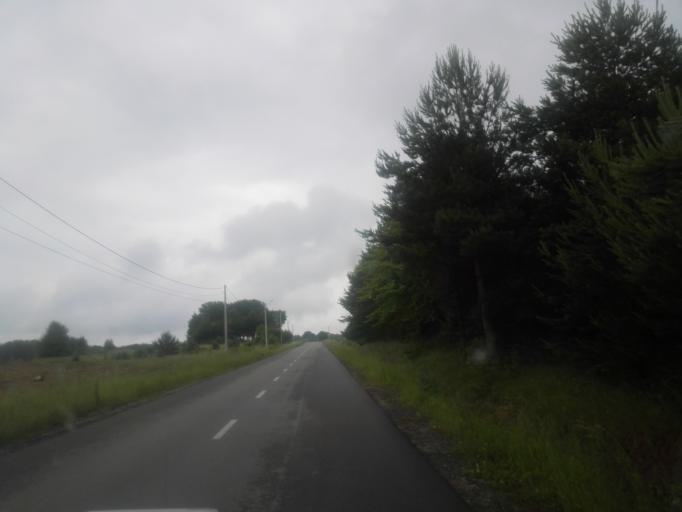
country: PL
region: Silesian Voivodeship
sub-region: Powiat czestochowski
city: Potok Zloty
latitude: 50.7009
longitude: 19.3622
